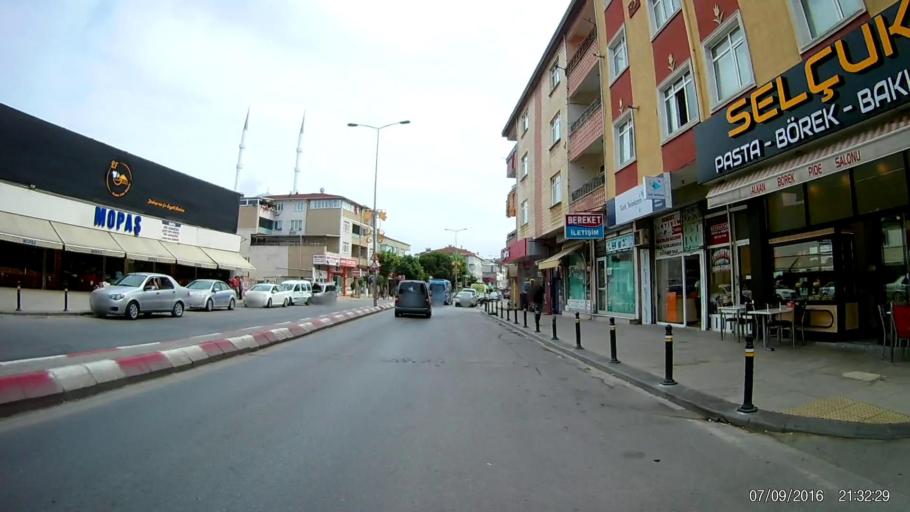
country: TR
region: Istanbul
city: Sultanbeyli
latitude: 40.9798
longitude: 29.2657
